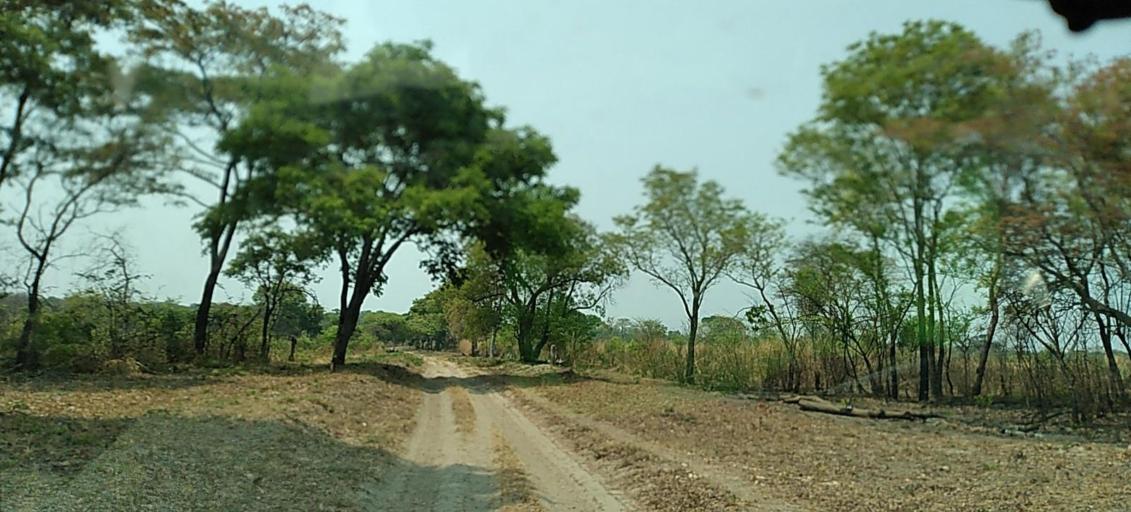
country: ZM
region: Western
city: Lukulu
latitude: -13.9653
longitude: 23.2266
